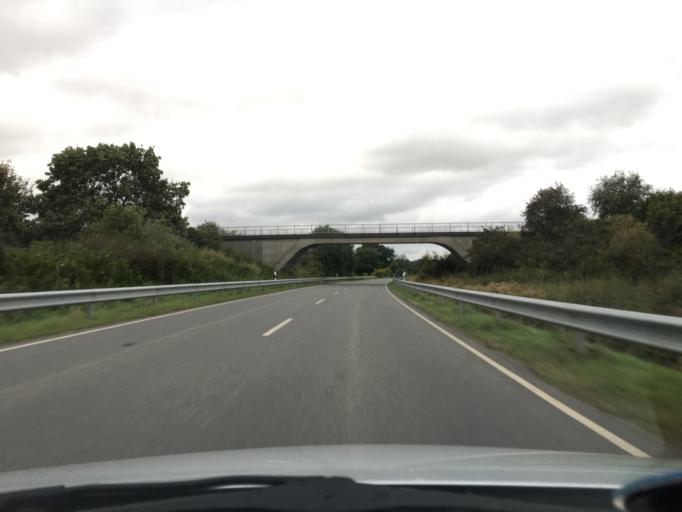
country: DE
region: Schleswig-Holstein
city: Osdorf
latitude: 54.4649
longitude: 10.0529
